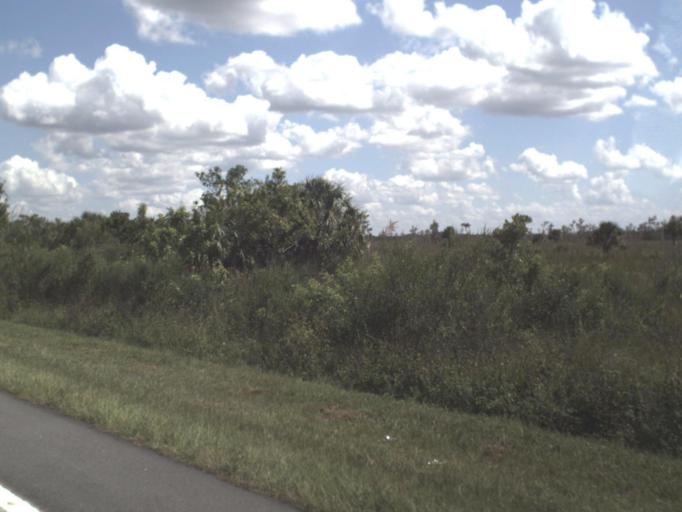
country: US
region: Florida
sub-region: Collier County
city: Lely Resort
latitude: 25.8668
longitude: -81.1311
